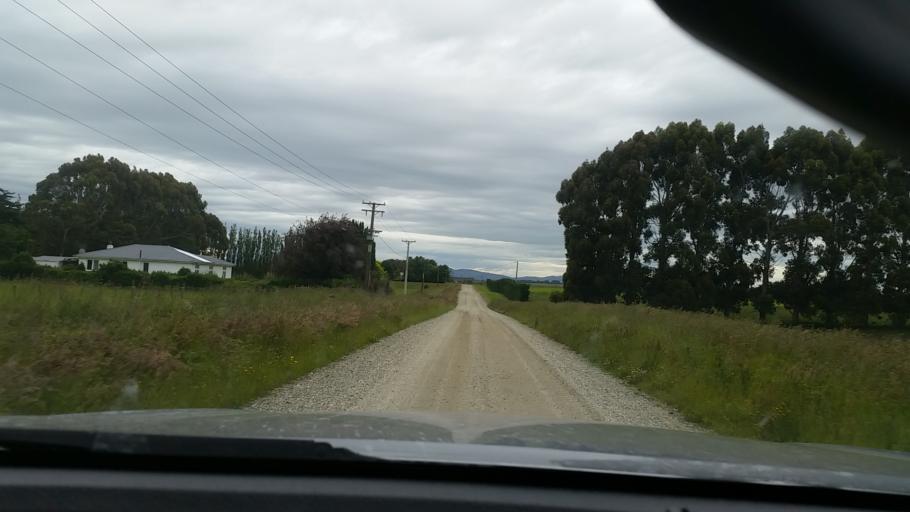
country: NZ
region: Southland
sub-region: Gore District
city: Gore
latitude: -46.3028
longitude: 168.7327
